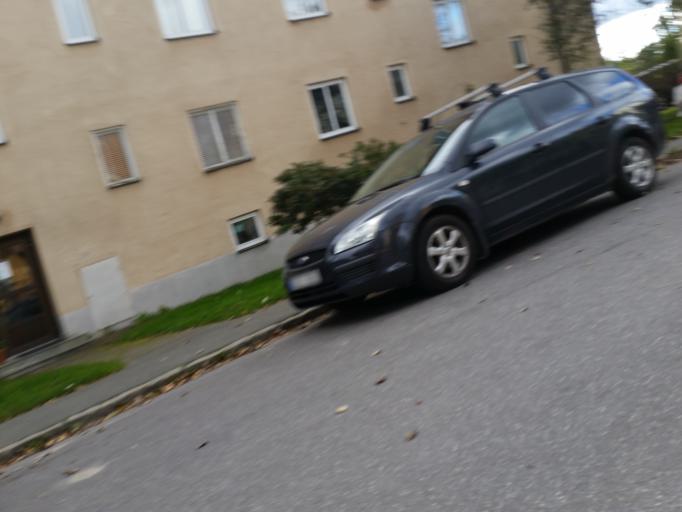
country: SE
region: Stockholm
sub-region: Stockholms Kommun
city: Arsta
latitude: 59.2923
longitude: 18.0989
